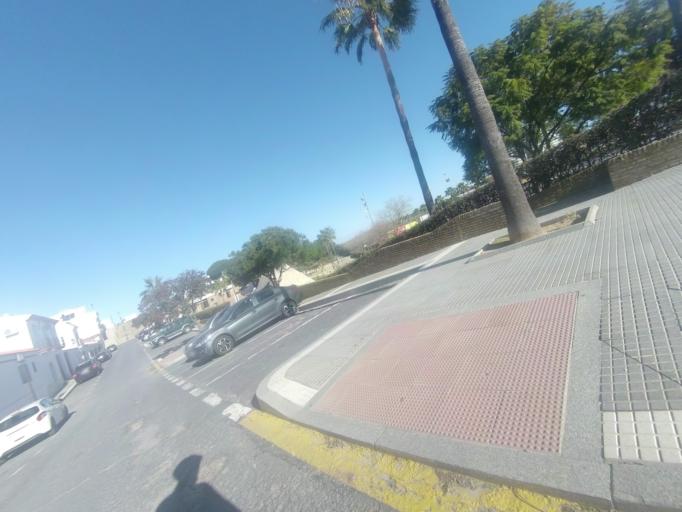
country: ES
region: Andalusia
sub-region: Provincia de Huelva
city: Palos de la Frontera
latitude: 37.2250
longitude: -6.8911
